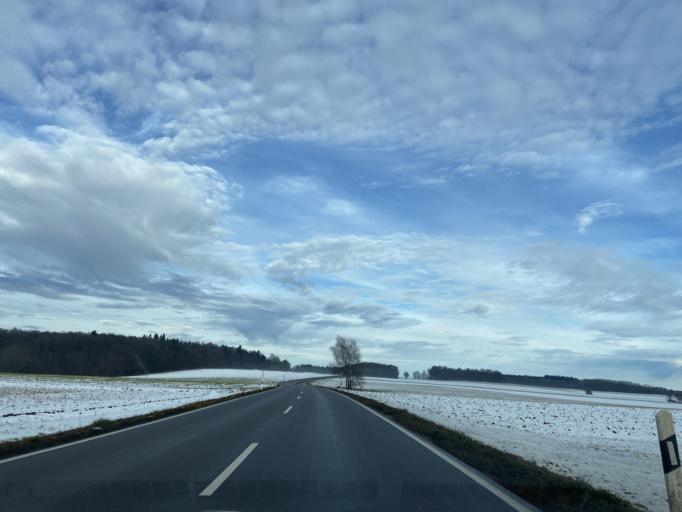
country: DE
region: Baden-Wuerttemberg
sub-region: Tuebingen Region
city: Hettingen
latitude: 48.2004
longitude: 9.2829
